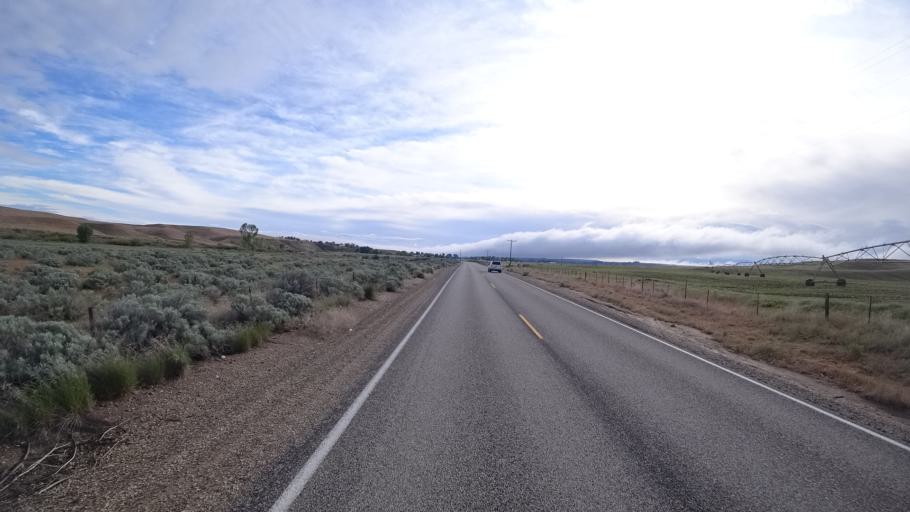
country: US
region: Idaho
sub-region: Ada County
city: Star
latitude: 43.7660
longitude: -116.4998
